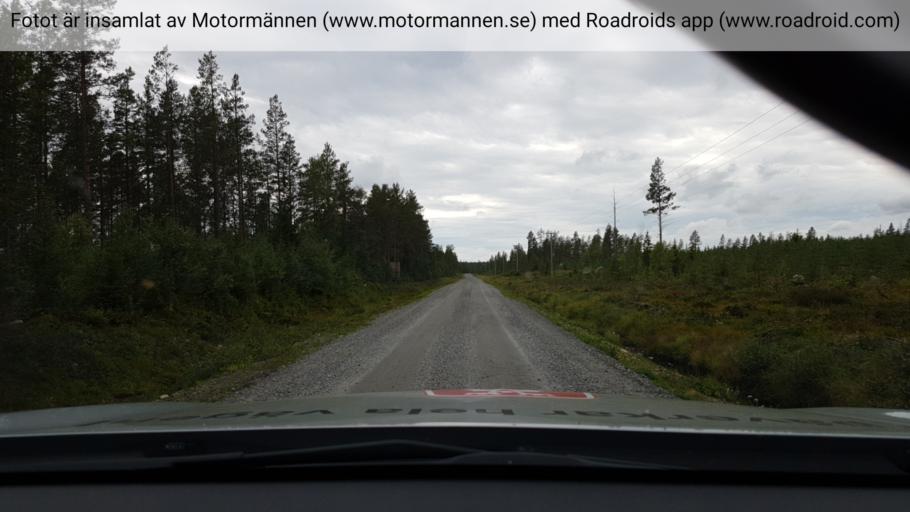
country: SE
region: Vaesterbotten
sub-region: Skelleftea Kommun
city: Langsele
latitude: 64.7335
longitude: 20.2924
